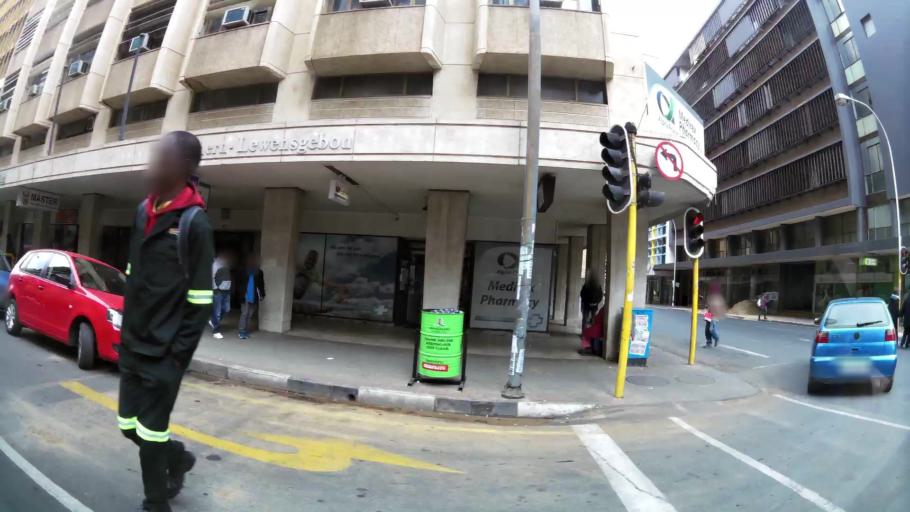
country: ZA
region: Orange Free State
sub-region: Mangaung Metropolitan Municipality
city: Bloemfontein
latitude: -29.1171
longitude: 26.2183
